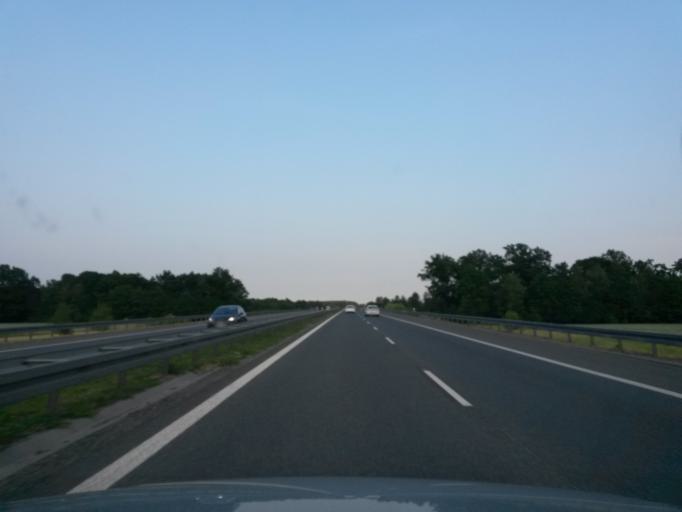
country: PL
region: Lower Silesian Voivodeship
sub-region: Powiat olesnicki
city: Olesnica
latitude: 51.2325
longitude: 17.4163
